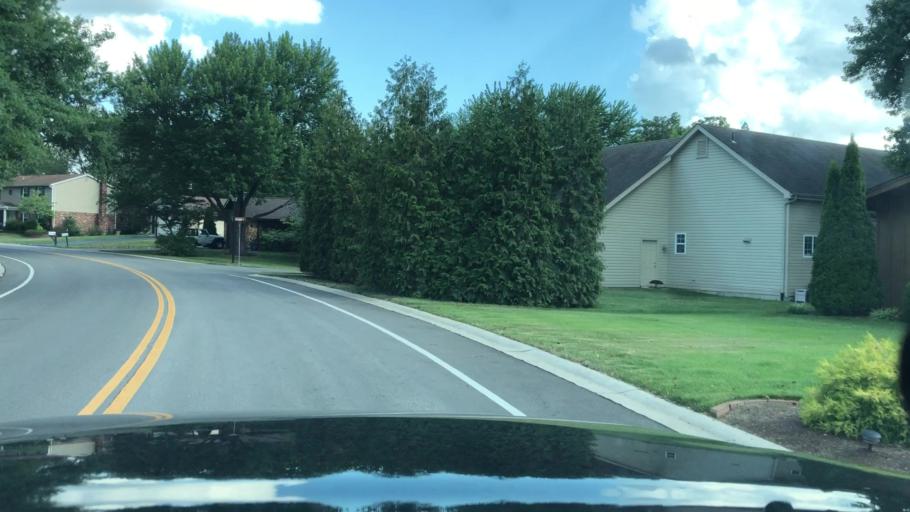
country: US
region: Missouri
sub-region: Saint Charles County
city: Lake Saint Louis
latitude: 38.7945
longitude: -90.8033
